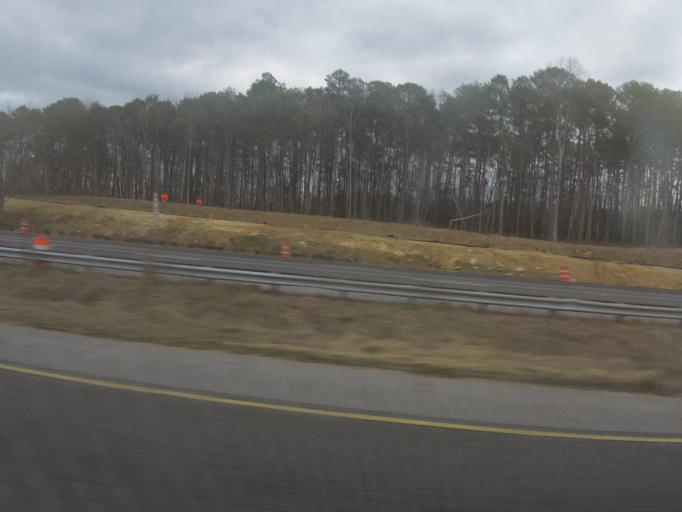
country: US
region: Georgia
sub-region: Whitfield County
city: Dalton
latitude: 34.6519
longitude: -84.9833
